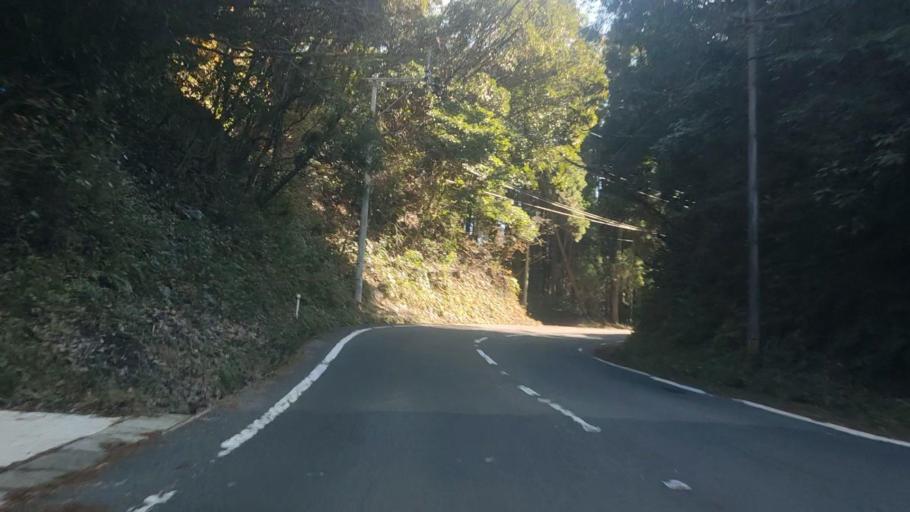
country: JP
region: Kagoshima
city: Kokubu-matsuki
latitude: 31.6694
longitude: 130.8369
